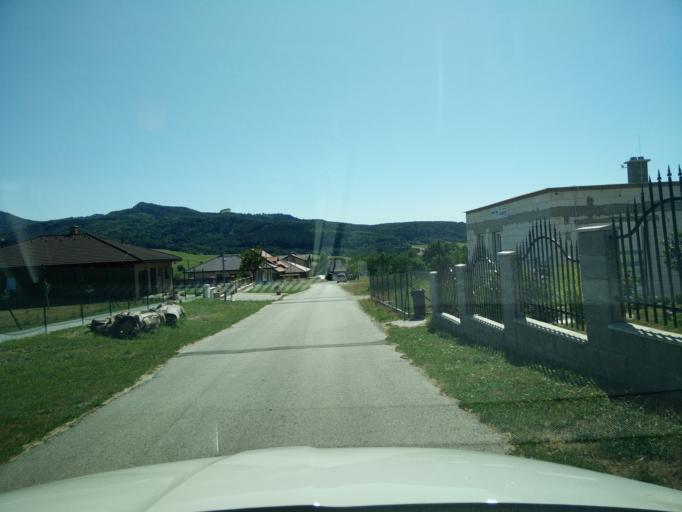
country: SK
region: Nitriansky
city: Handlova
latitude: 48.7838
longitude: 18.7147
